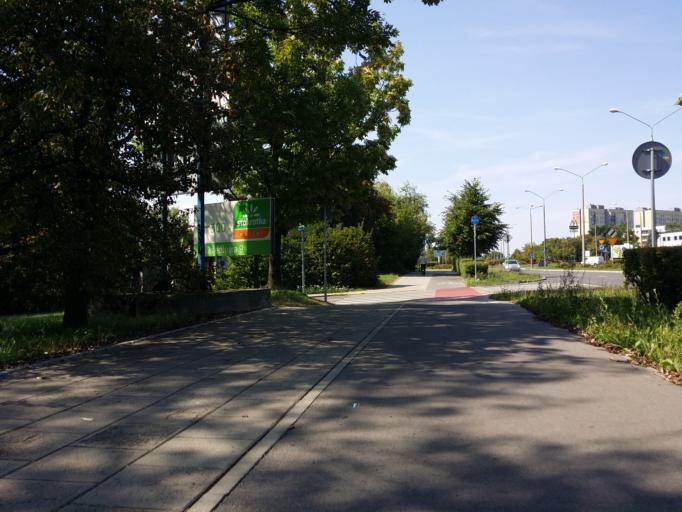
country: PL
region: Masovian Voivodeship
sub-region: Radom
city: Radom
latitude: 51.3835
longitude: 21.1628
